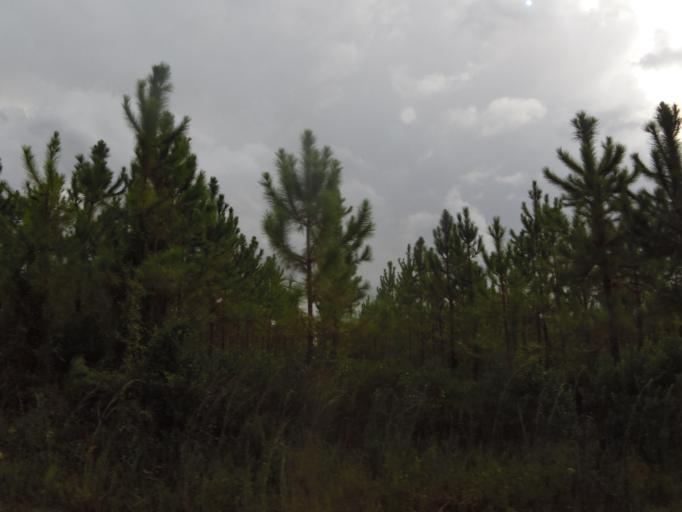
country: US
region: Florida
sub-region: Nassau County
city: Hilliard
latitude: 30.5942
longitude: -82.0530
